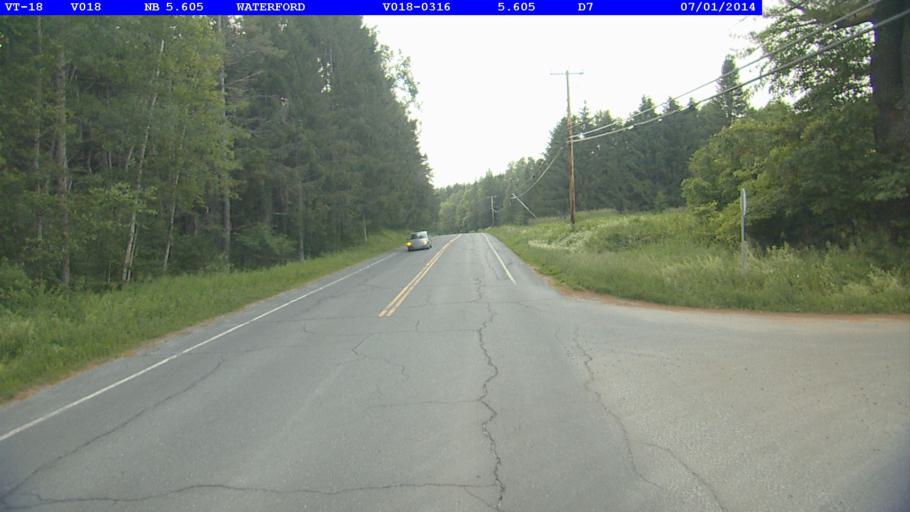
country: US
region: Vermont
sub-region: Caledonia County
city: Saint Johnsbury
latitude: 44.4106
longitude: -71.9312
